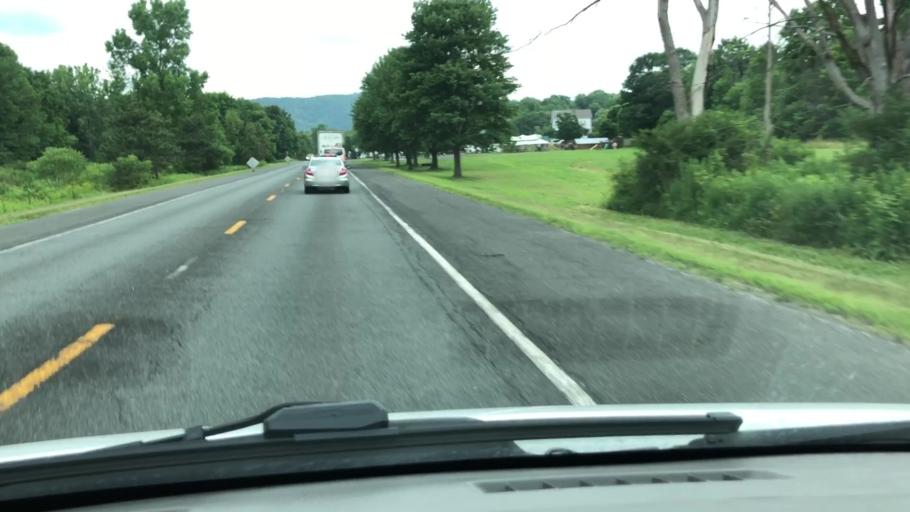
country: US
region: Massachusetts
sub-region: Berkshire County
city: Lanesborough
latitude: 42.5193
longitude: -73.1924
